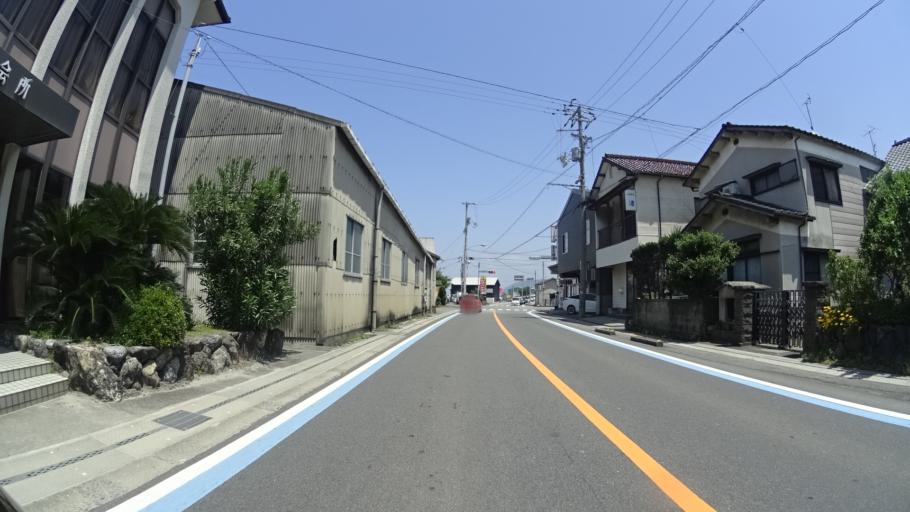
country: JP
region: Ehime
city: Iyo
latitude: 33.6878
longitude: 132.6369
